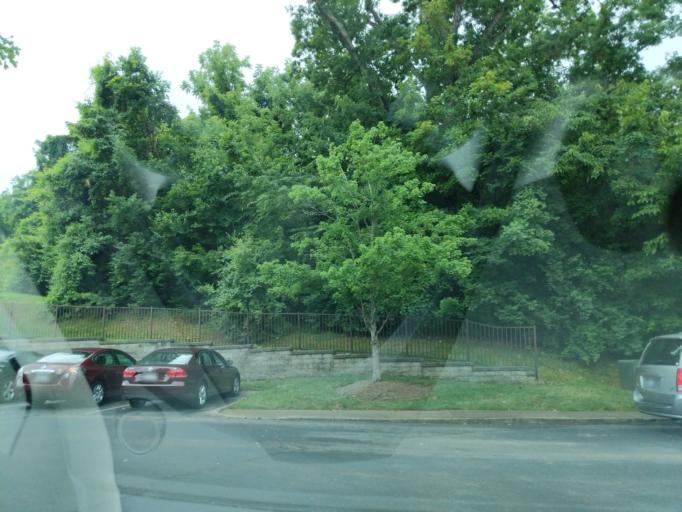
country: US
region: Tennessee
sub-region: Davidson County
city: Lakewood
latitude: 36.1711
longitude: -86.6096
